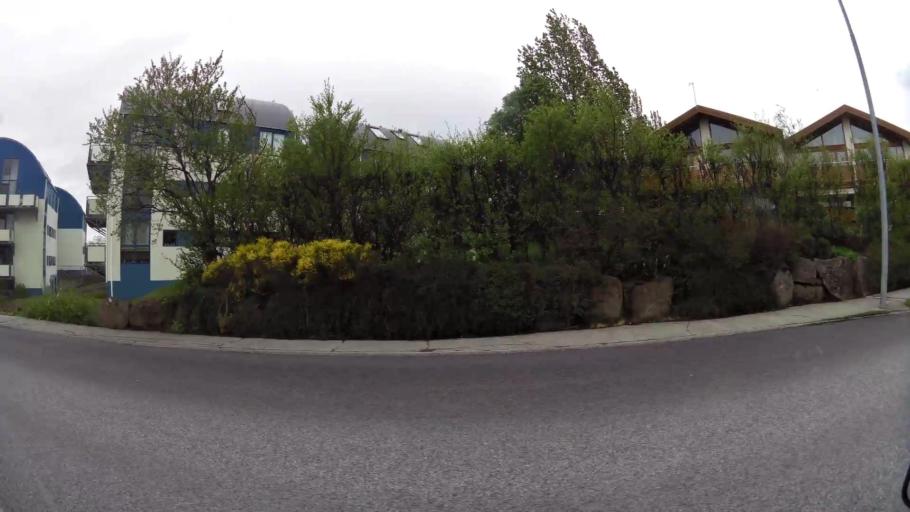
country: IS
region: Capital Region
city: Hafnarfjoerdur
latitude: 64.0658
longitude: -21.9319
